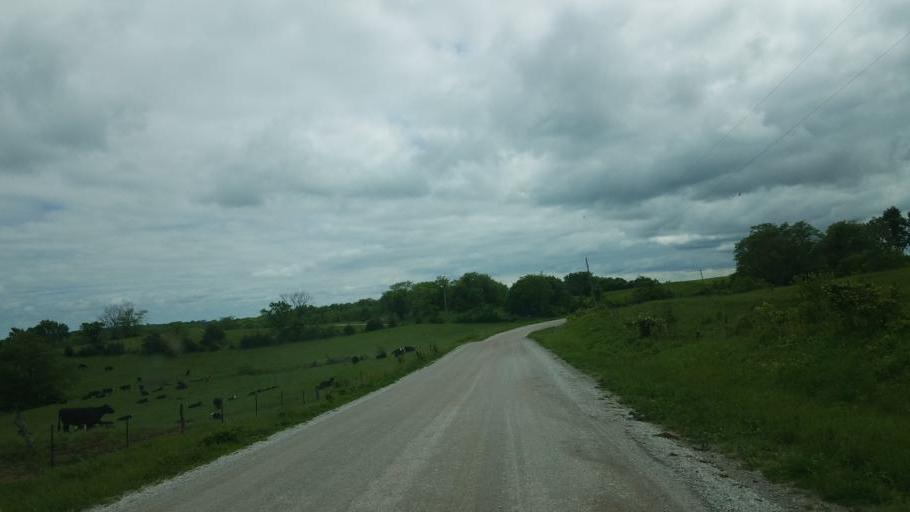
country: US
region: Iowa
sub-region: Decatur County
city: Lamoni
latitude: 40.5967
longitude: -93.8443
